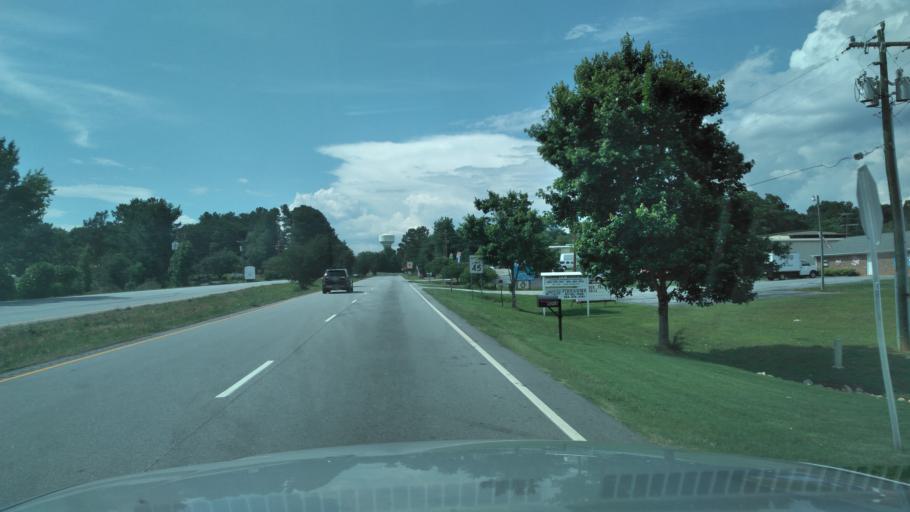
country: US
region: South Carolina
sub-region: Spartanburg County
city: Roebuck
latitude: 34.8842
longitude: -81.9575
